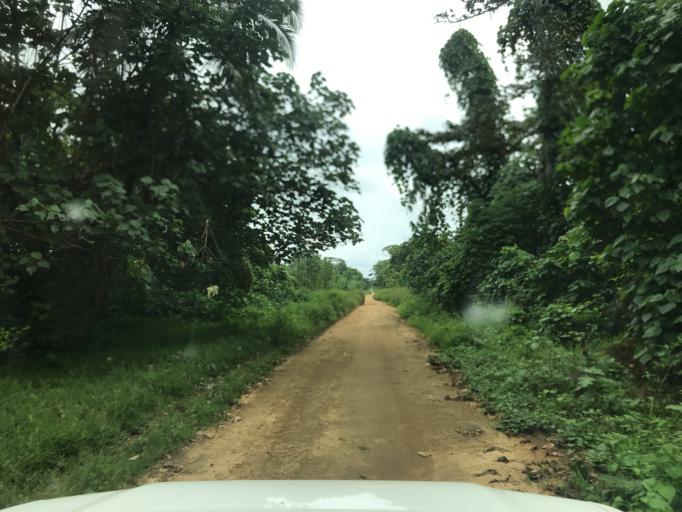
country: VU
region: Sanma
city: Port-Olry
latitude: -15.1849
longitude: 167.0302
